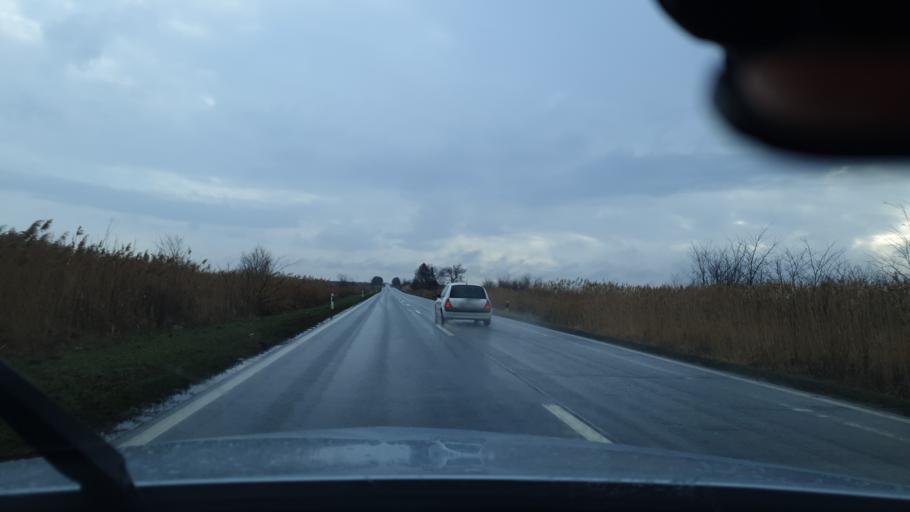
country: RS
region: Autonomna Pokrajina Vojvodina
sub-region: Juznobanatski Okrug
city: Kovin
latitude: 44.8347
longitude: 20.8186
